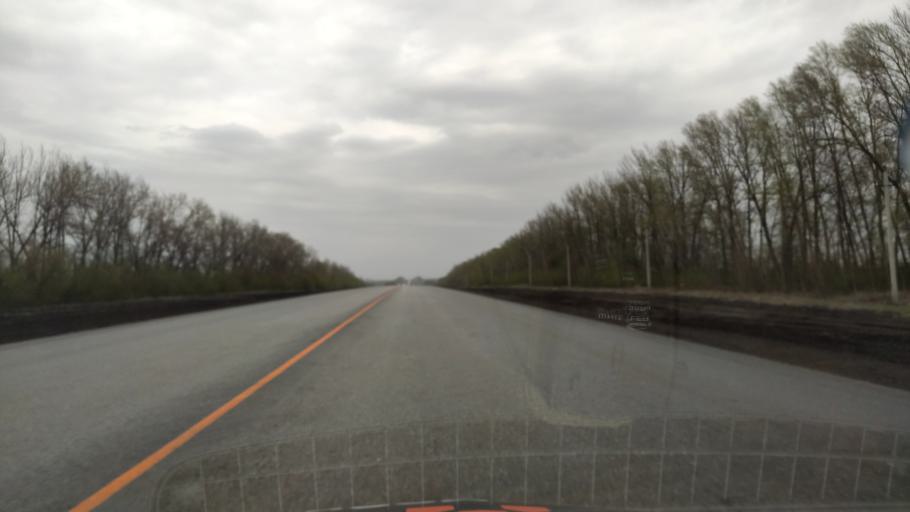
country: RU
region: Kursk
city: Gorshechnoye
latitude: 51.5477
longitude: 38.0835
